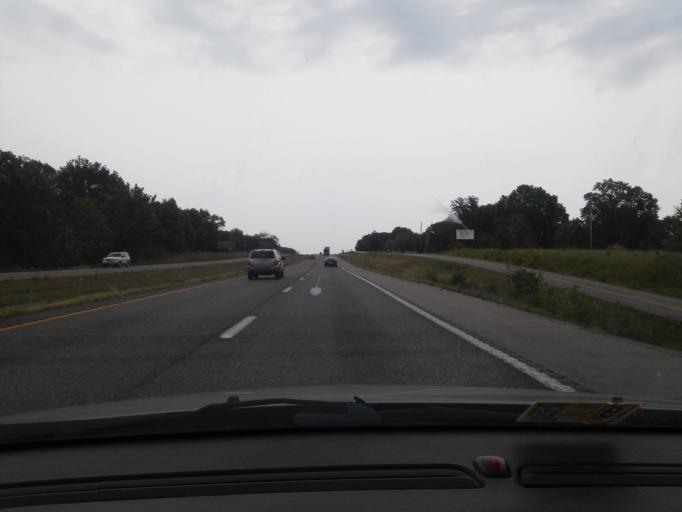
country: US
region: Missouri
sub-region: Boone County
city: Columbia
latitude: 38.9579
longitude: -92.1722
